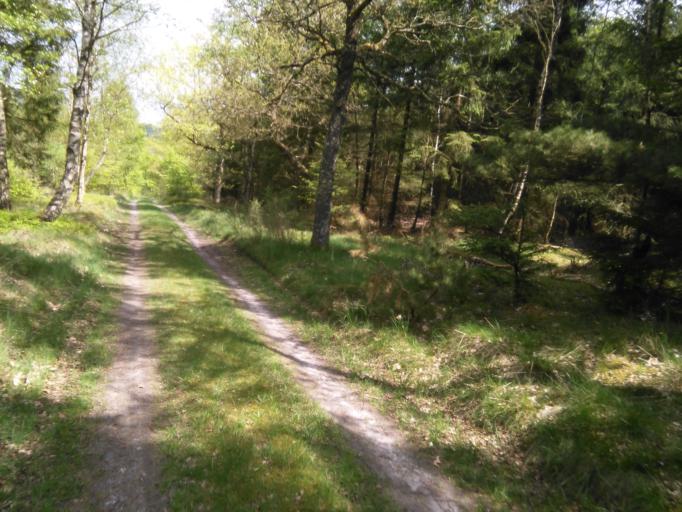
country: DK
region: Central Jutland
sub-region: Silkeborg Kommune
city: Svejbaek
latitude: 56.0596
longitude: 9.6385
